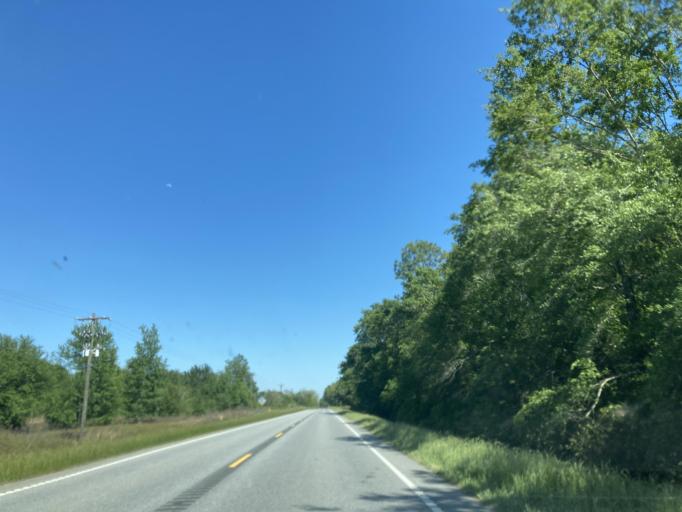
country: US
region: Georgia
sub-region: Miller County
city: Colquitt
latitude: 31.1836
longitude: -84.5528
